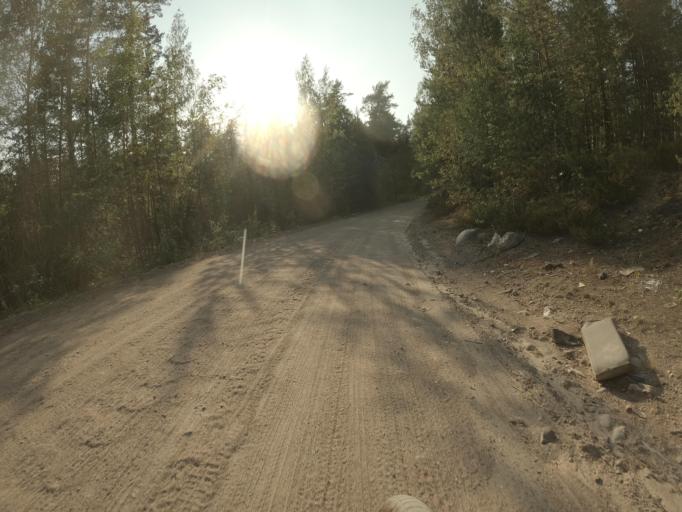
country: RU
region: Leningrad
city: Veshchevo
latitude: 60.4621
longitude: 29.2399
